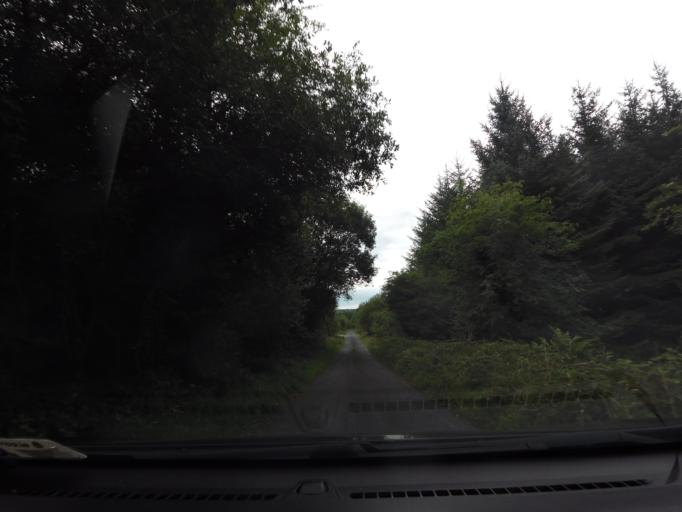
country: IE
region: Connaught
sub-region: County Galway
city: Loughrea
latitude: 53.1352
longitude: -8.5205
